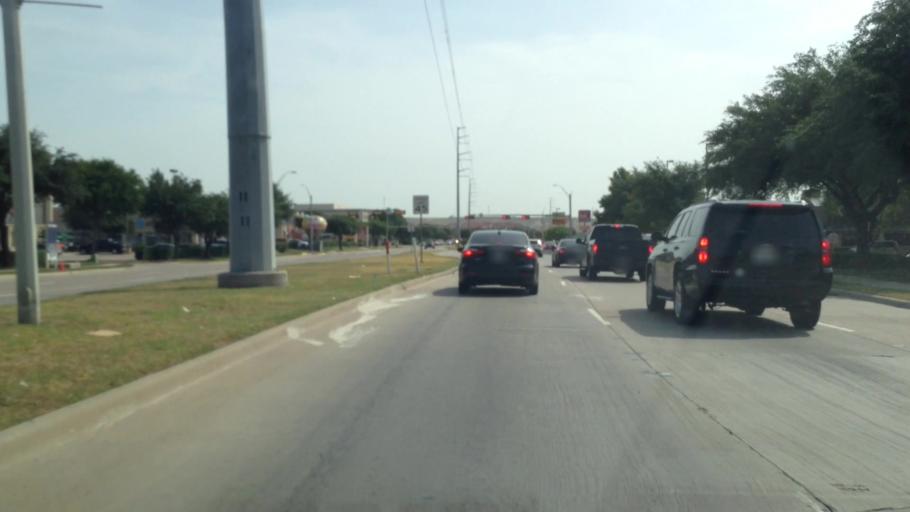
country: US
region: Texas
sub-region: Denton County
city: Lewisville
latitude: 33.0091
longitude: -96.9698
